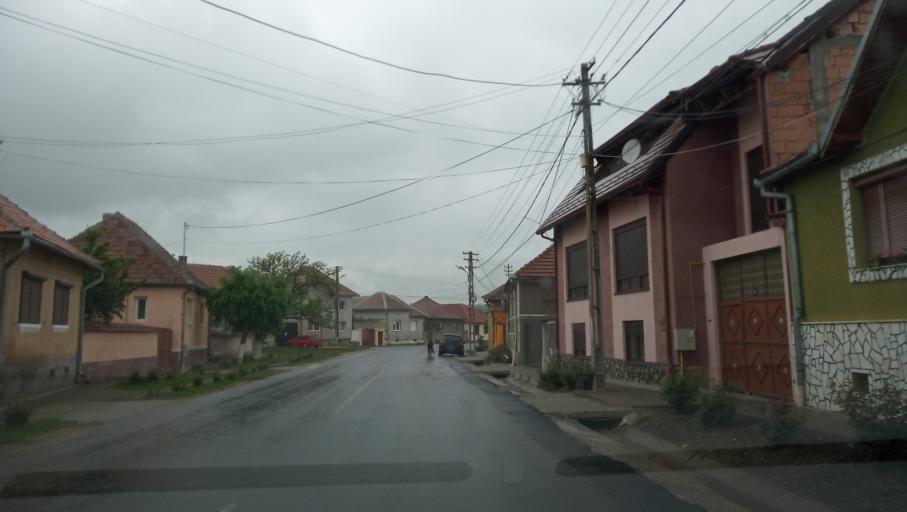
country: RO
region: Sibiu
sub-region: Comuna Selimbar
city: Vestem
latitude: 45.7195
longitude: 24.2328
